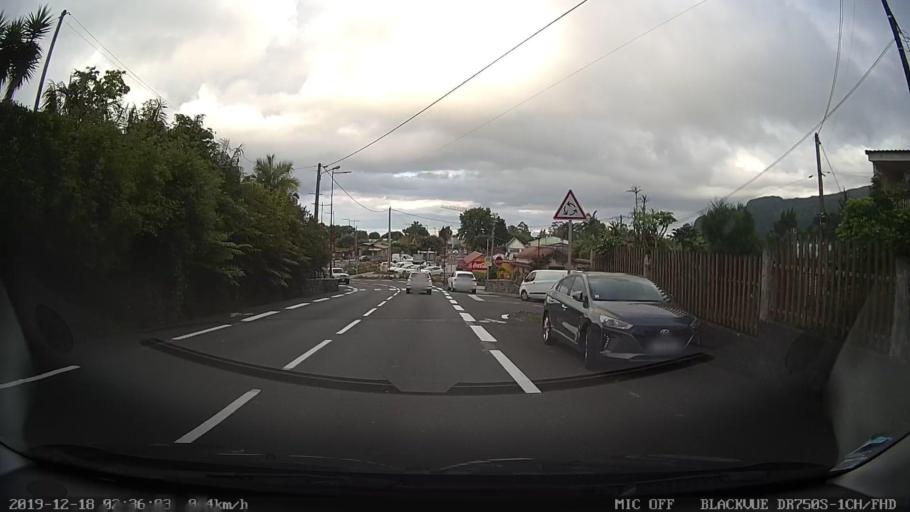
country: RE
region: Reunion
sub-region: Reunion
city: Salazie
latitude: -21.1441
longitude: 55.6199
